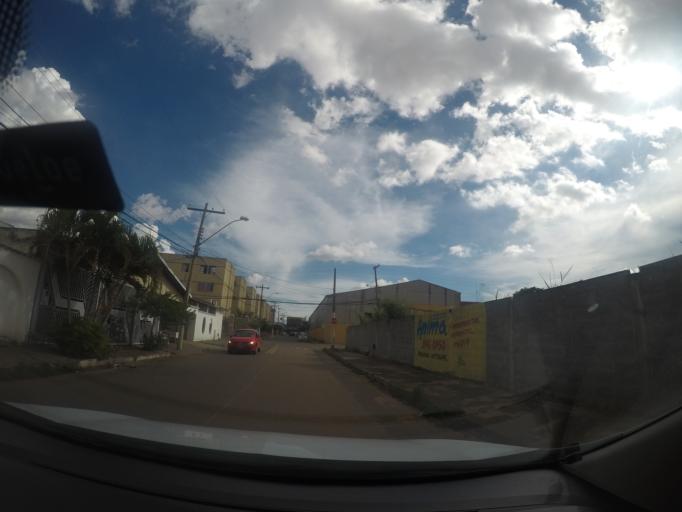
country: BR
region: Goias
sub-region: Goiania
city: Goiania
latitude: -16.6734
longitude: -49.3052
